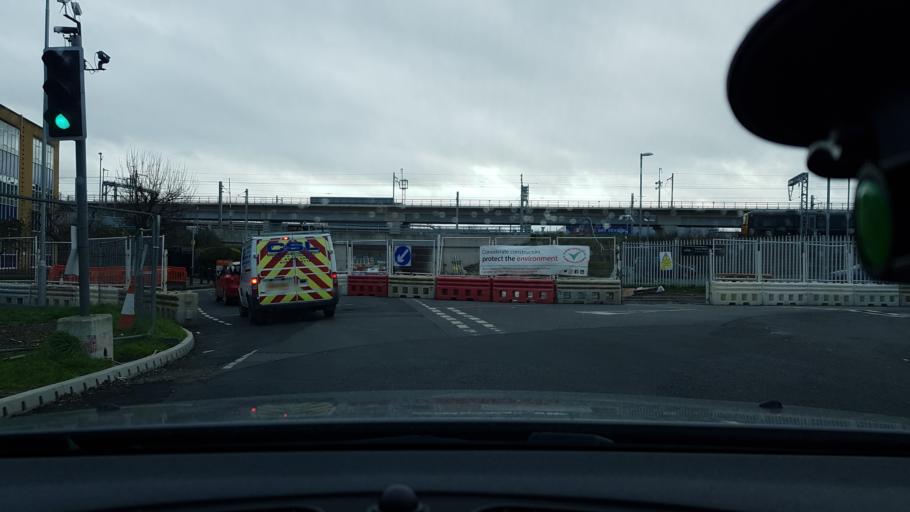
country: GB
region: England
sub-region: Reading
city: Reading
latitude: 51.4622
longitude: -0.9887
